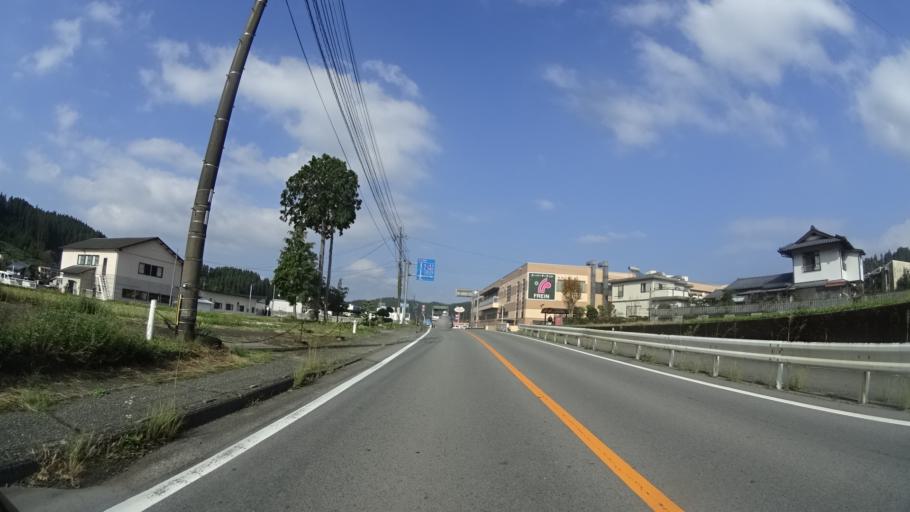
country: JP
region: Oita
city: Tsukawaki
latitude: 33.1201
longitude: 131.0601
